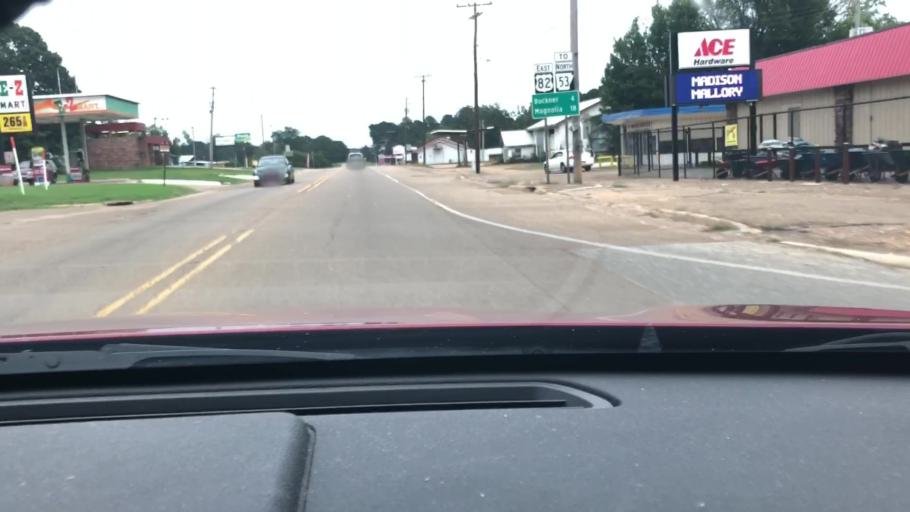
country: US
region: Arkansas
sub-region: Lafayette County
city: Stamps
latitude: 33.3653
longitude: -93.4889
